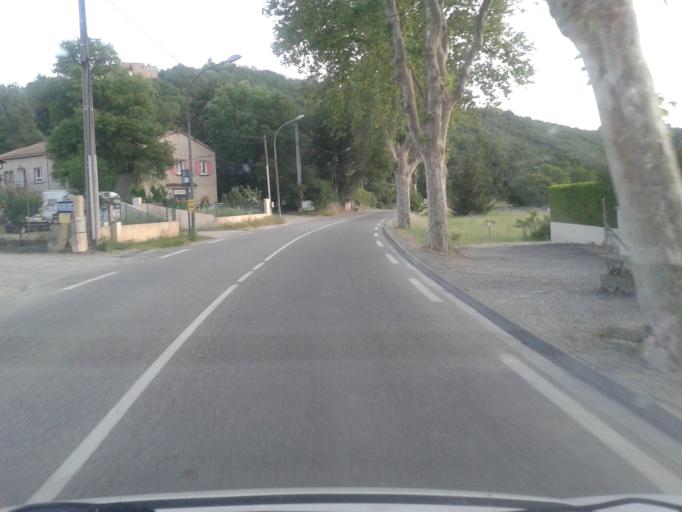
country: FR
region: Provence-Alpes-Cote d'Azur
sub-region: Departement du Var
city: Vinon-sur-Verdon
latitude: 43.7210
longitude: 5.8100
